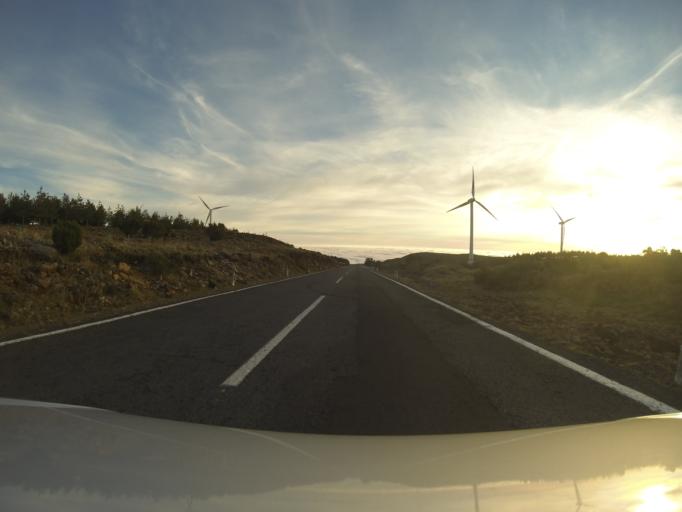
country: PT
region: Madeira
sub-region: Sao Vicente
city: Sao Vicente
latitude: 32.7396
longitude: -17.0596
